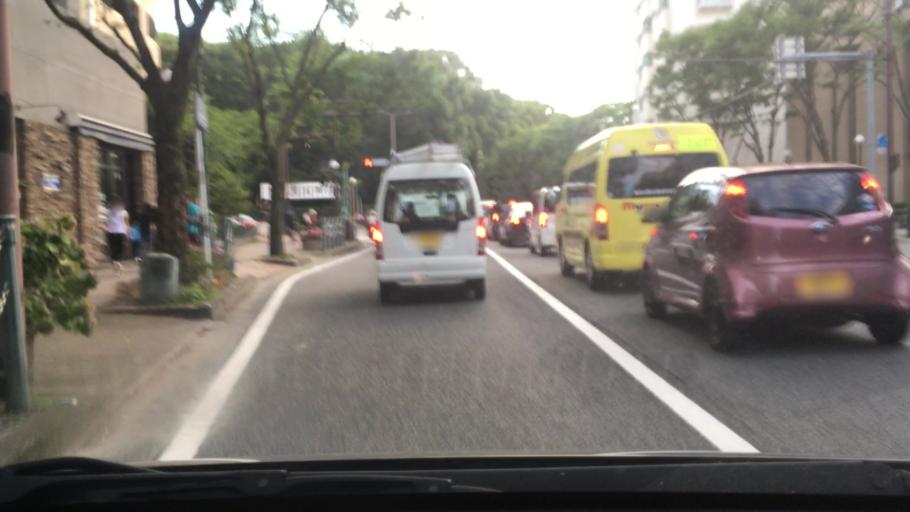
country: JP
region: Fukuoka
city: Fukuoka-shi
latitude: 33.5830
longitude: 130.3840
